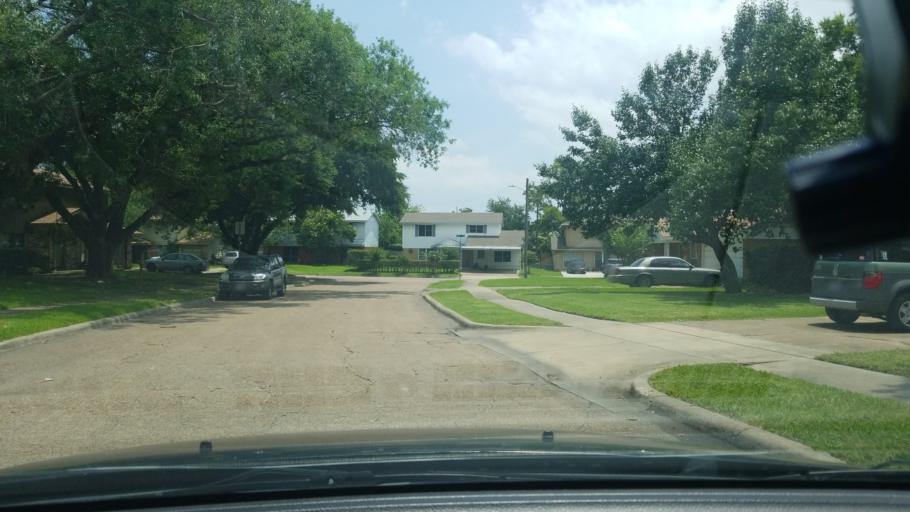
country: US
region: Texas
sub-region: Dallas County
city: Mesquite
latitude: 32.7946
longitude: -96.6418
